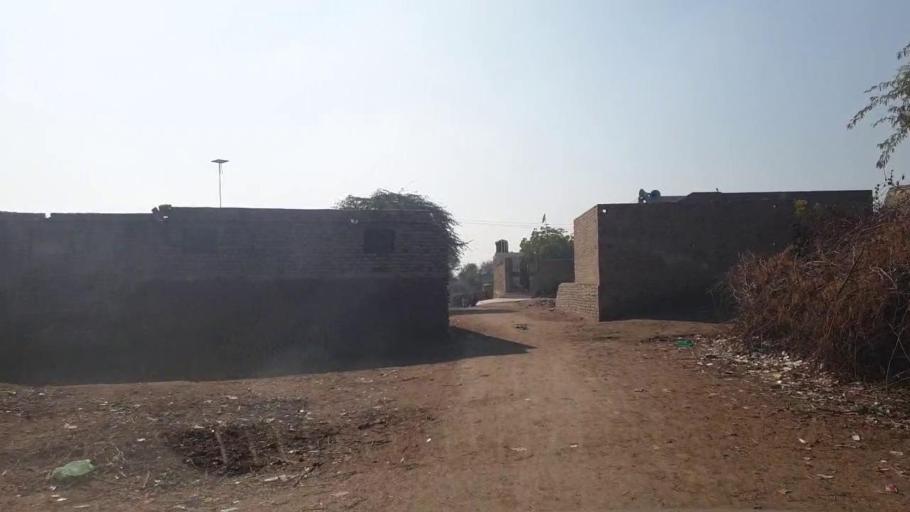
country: PK
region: Sindh
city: Shahdadpur
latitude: 25.9628
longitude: 68.5791
